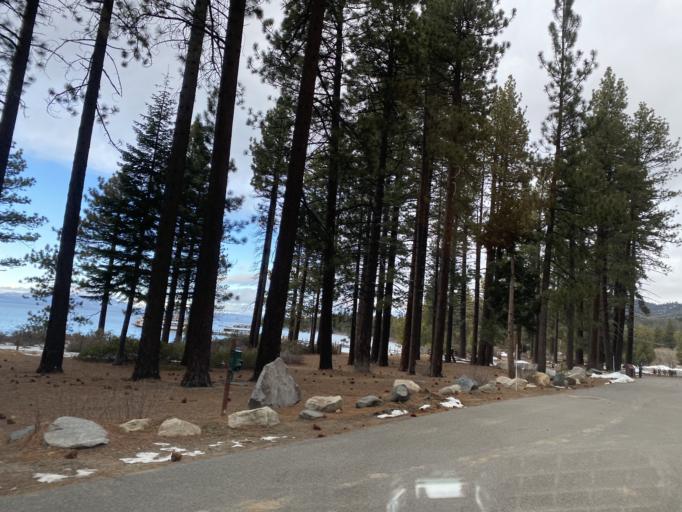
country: US
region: Nevada
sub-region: Douglas County
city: Kingsbury
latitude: 39.0050
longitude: -119.9489
